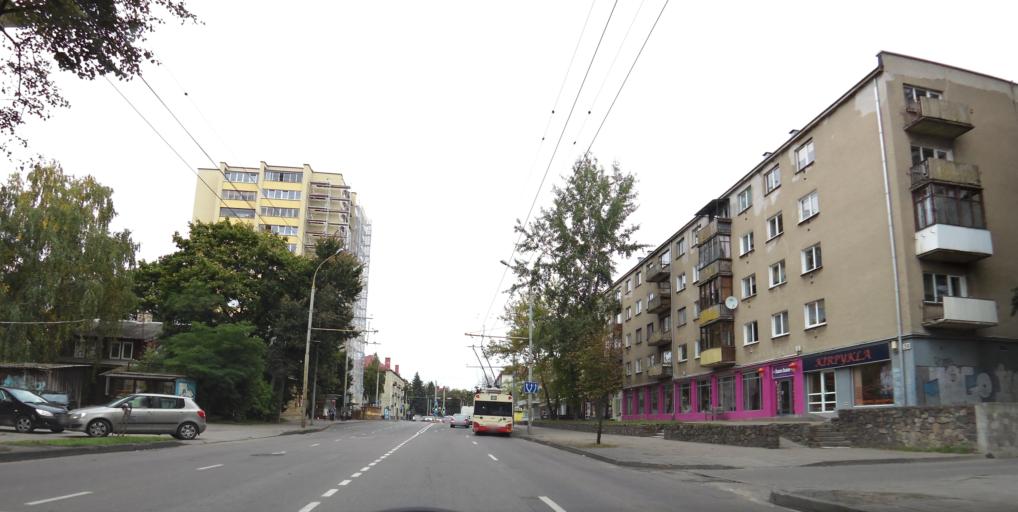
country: LT
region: Vilnius County
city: Rasos
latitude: 54.7038
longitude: 25.3101
